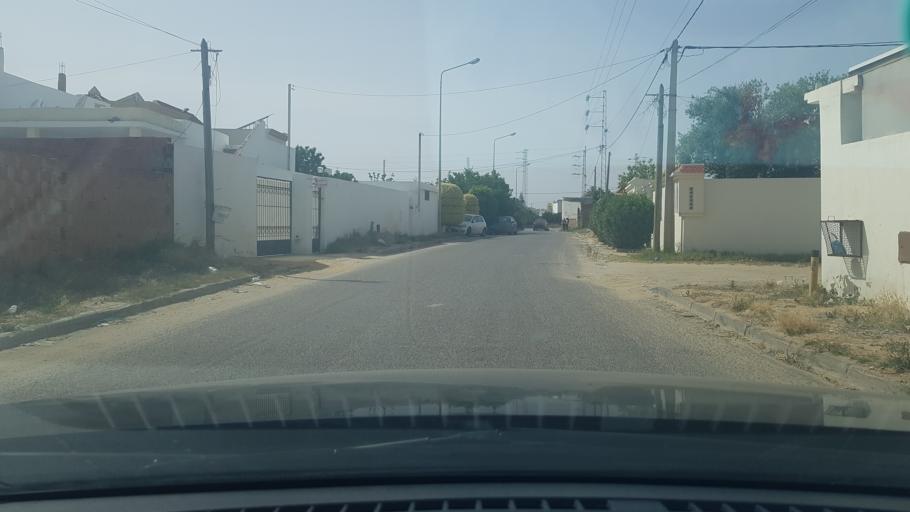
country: TN
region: Safaqis
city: Al Qarmadah
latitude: 34.8060
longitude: 10.7673
